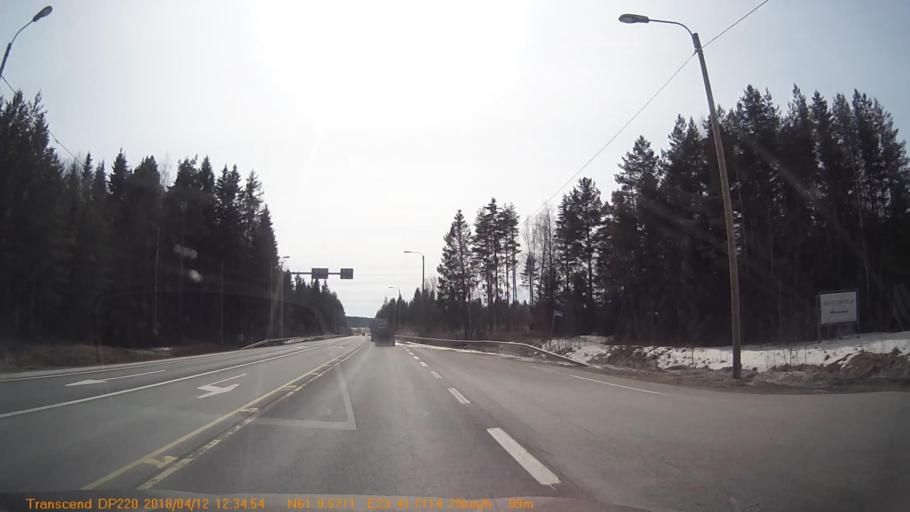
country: FI
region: Pirkanmaa
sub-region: Etelae-Pirkanmaa
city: Kylmaekoski
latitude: 61.1596
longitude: 23.6952
